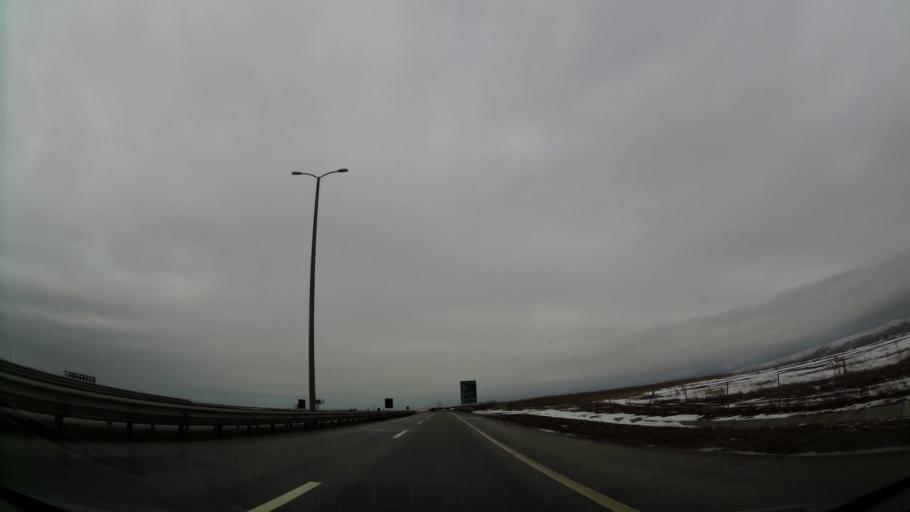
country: XK
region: Pristina
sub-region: Kosovo Polje
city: Kosovo Polje
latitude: 42.6261
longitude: 21.1313
